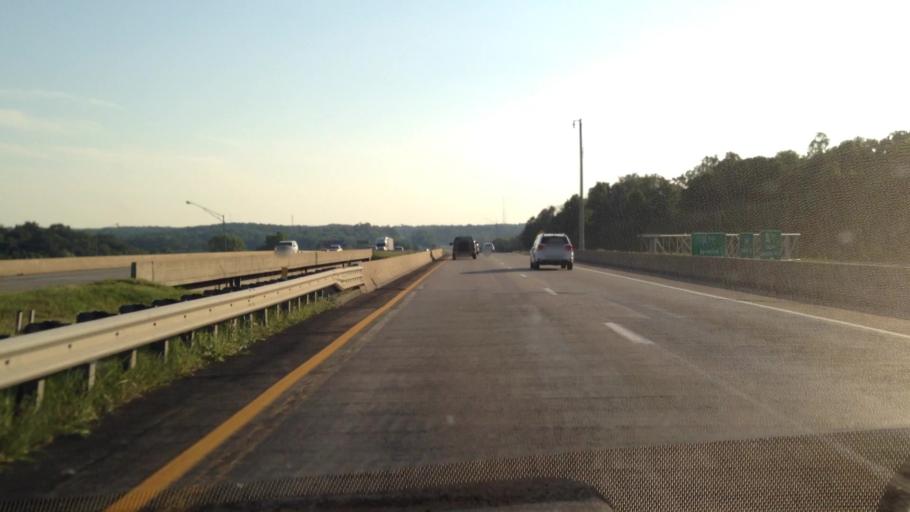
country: US
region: Missouri
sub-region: Jasper County
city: Joplin
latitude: 37.0368
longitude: -94.5142
